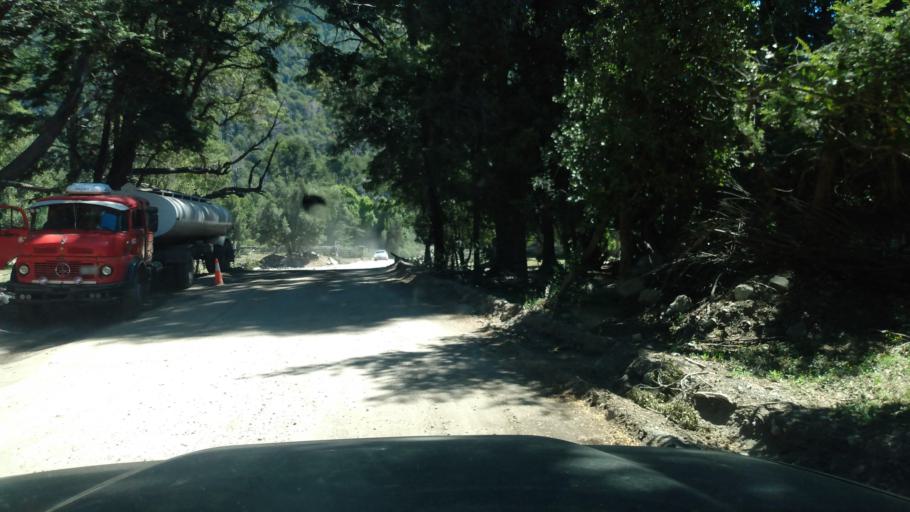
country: AR
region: Neuquen
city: Villa La Angostura
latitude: -40.6225
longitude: -71.5156
